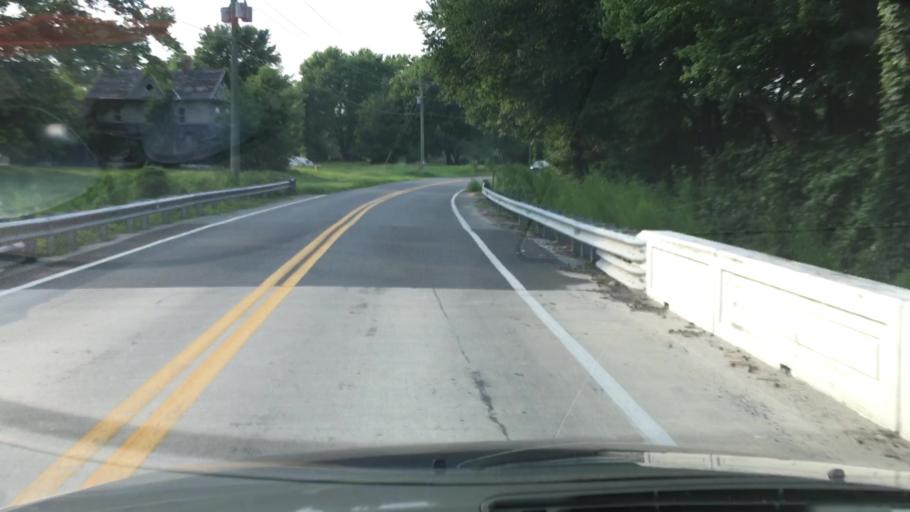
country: US
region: Maryland
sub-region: Worcester County
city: Ocean Pines
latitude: 38.4755
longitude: -75.1396
